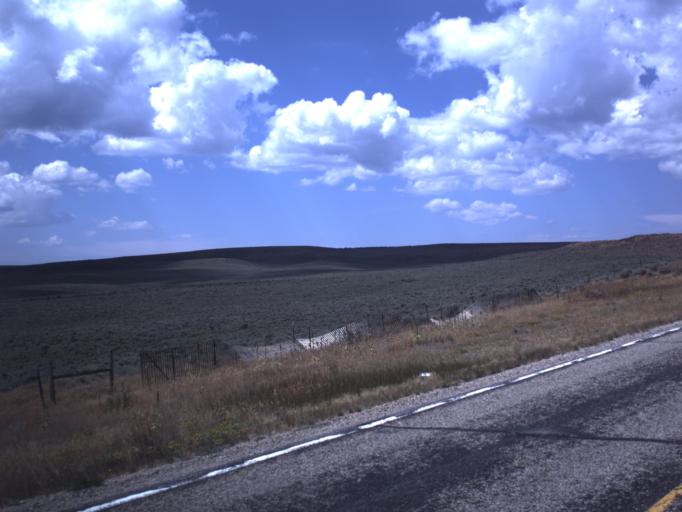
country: US
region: Utah
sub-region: Rich County
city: Randolph
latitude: 41.7958
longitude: -111.2332
